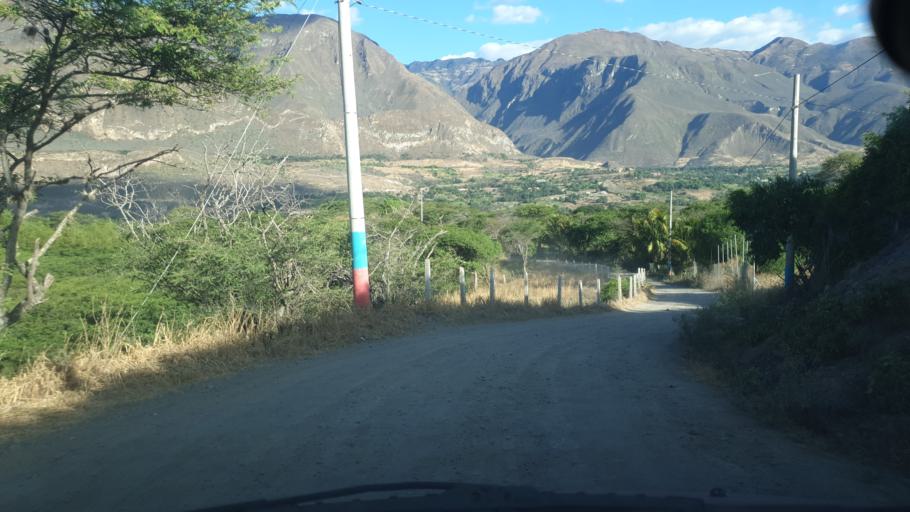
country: EC
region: Azuay
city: Cuenca
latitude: -3.2917
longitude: -79.2860
